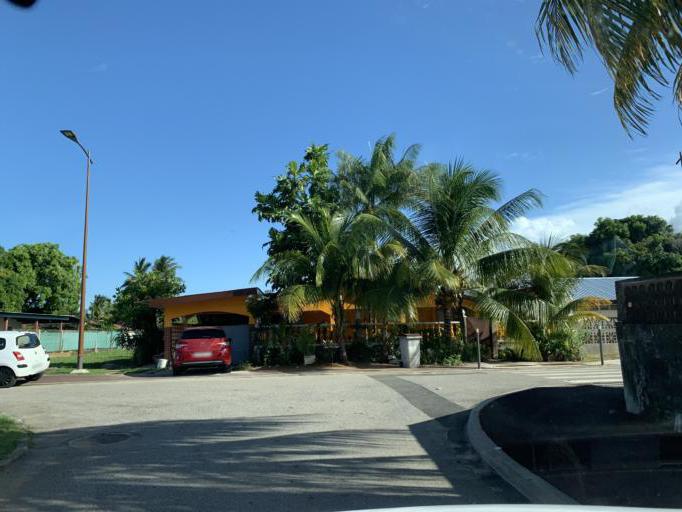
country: GF
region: Guyane
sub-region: Guyane
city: Kourou
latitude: 5.1723
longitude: -52.6457
